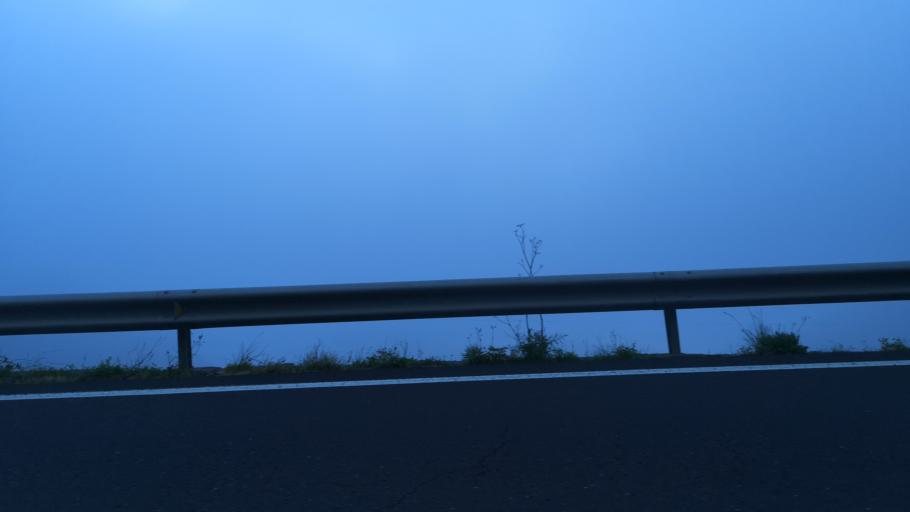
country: ES
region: Canary Islands
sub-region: Provincia de Santa Cruz de Tenerife
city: Alajero
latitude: 28.0941
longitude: -17.1903
